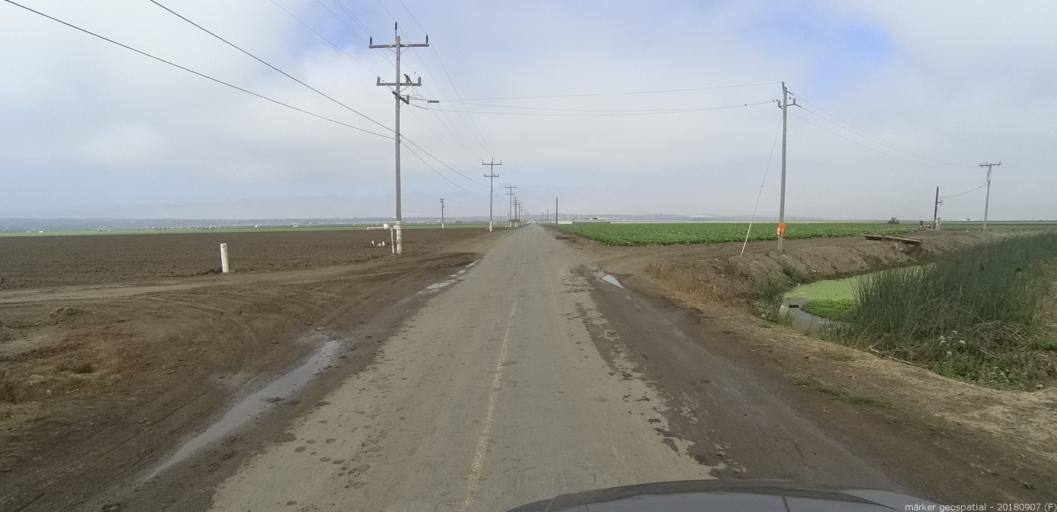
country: US
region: California
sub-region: Monterey County
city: Boronda
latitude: 36.6933
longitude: -121.7148
